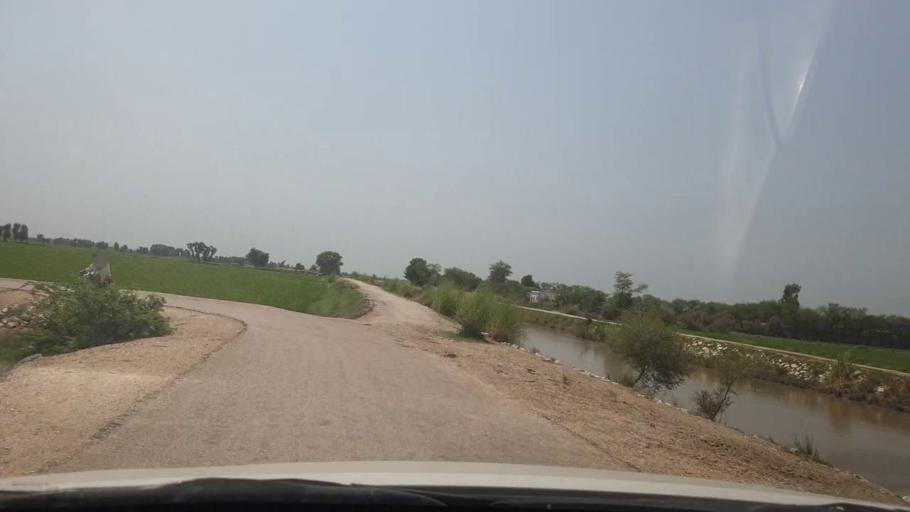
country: PK
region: Sindh
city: Rustam jo Goth
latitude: 28.0232
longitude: 68.8000
